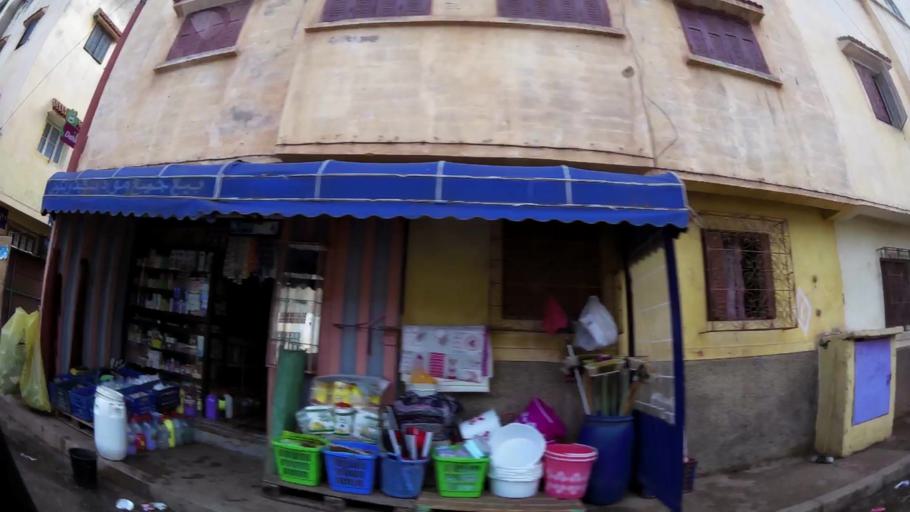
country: MA
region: Grand Casablanca
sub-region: Mohammedia
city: Mohammedia
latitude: 33.6806
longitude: -7.3776
